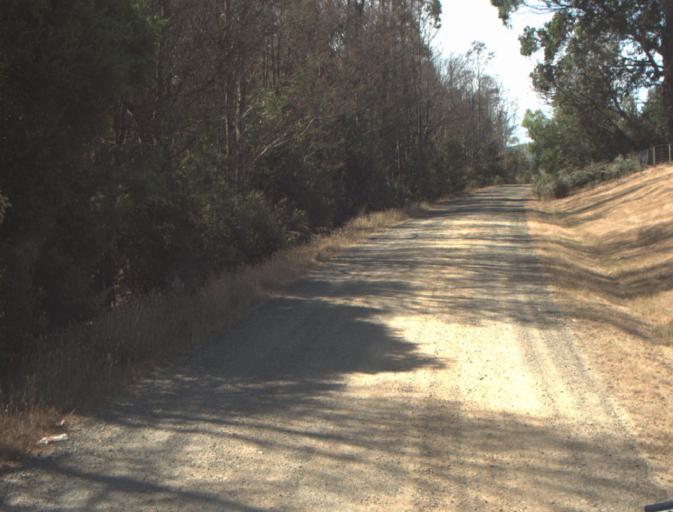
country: AU
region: Tasmania
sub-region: Launceston
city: Mayfield
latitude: -41.2218
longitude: 147.2436
